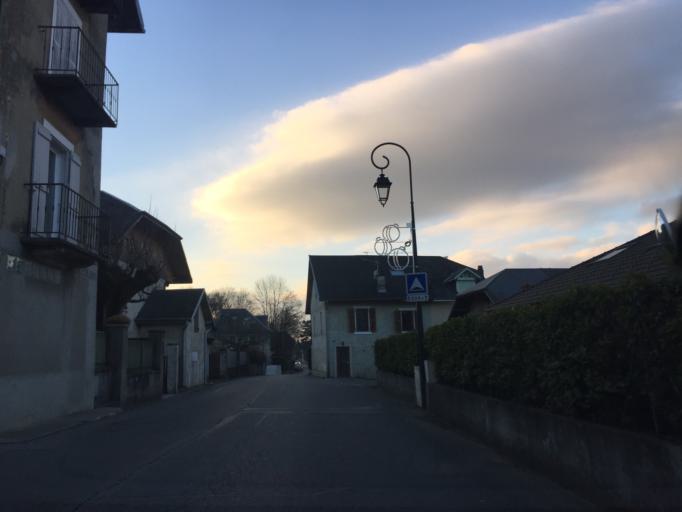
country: FR
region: Rhone-Alpes
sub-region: Departement de la Savoie
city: Tresserve
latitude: 45.6751
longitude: 5.8998
